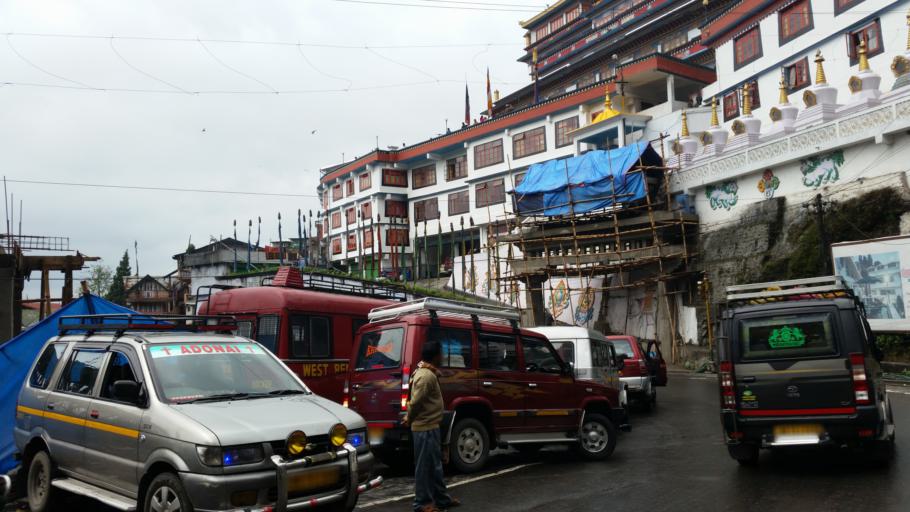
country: IN
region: West Bengal
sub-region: Darjiling
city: Darjiling
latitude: 27.0231
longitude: 88.2549
